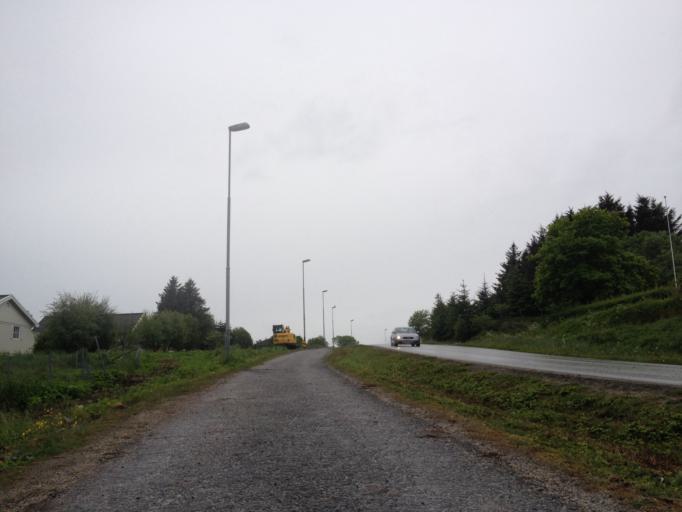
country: NO
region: Sor-Trondelag
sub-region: Froya
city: Sistranda
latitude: 63.6987
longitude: 8.8031
